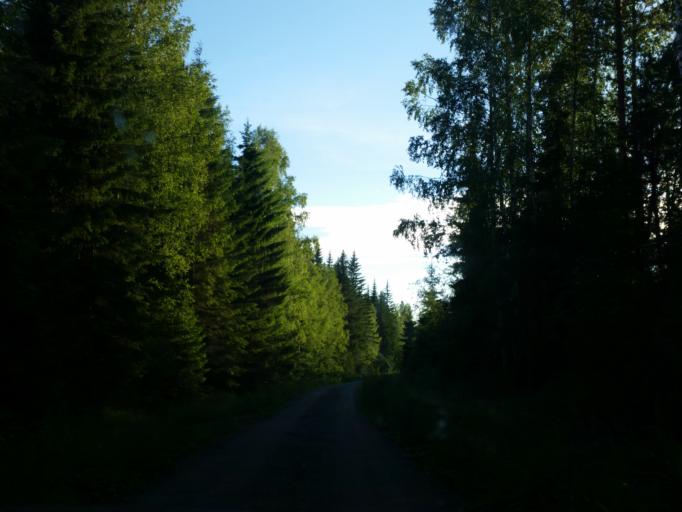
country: FI
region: Northern Savo
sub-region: Sisae-Savo
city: Tervo
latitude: 63.0562
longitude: 26.6793
